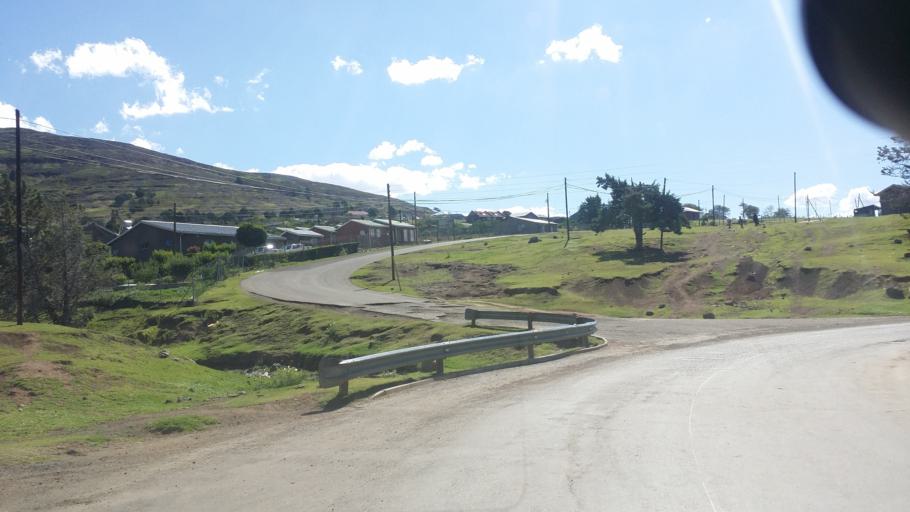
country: LS
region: Mokhotlong
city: Mokhotlong
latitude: -29.2904
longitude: 29.0730
